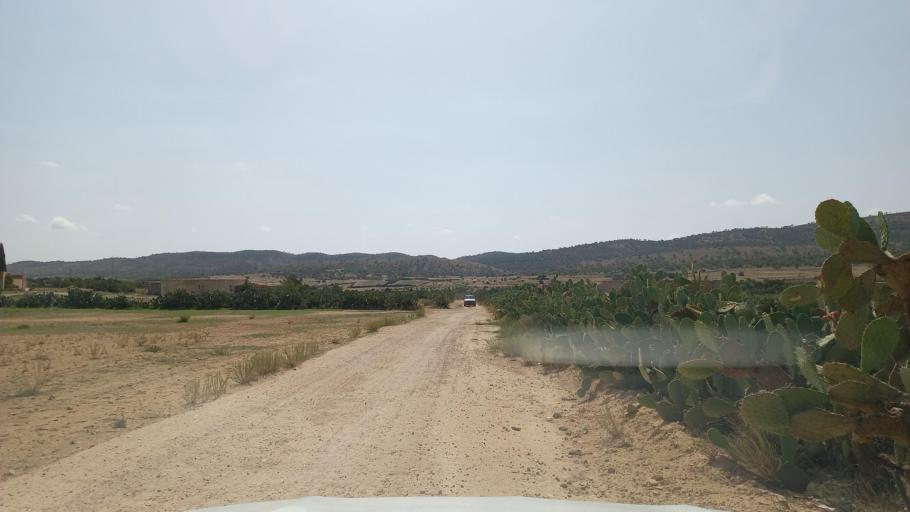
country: TN
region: Al Qasrayn
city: Sbiba
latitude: 35.3878
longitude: 8.9561
